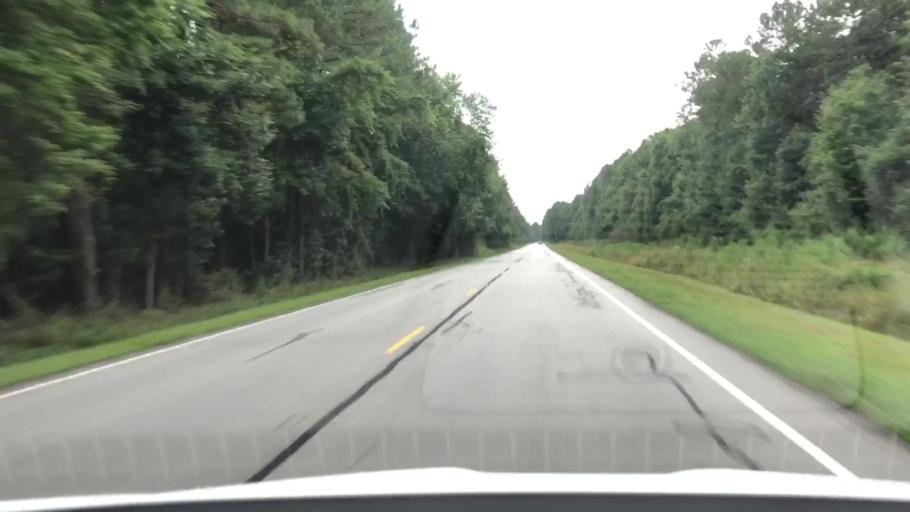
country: US
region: North Carolina
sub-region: Jones County
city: Trenton
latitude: 35.1133
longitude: -77.5093
